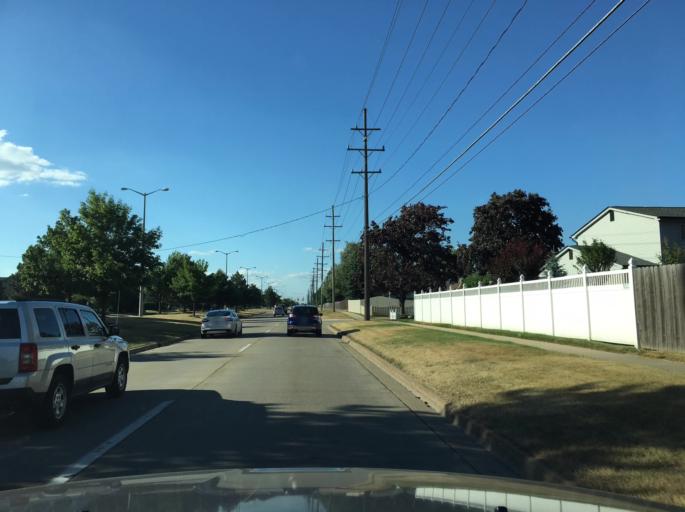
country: US
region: Michigan
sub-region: Macomb County
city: Utica
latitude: 42.6063
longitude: -82.9918
